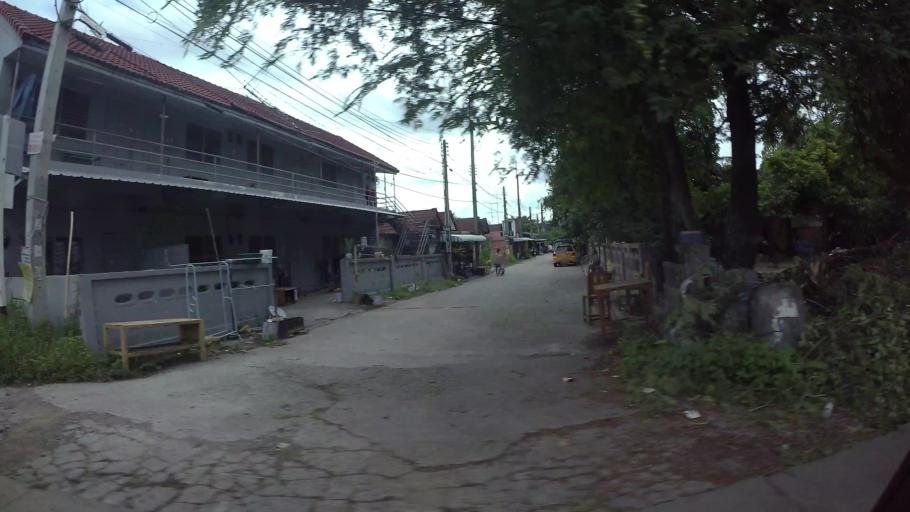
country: TH
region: Chon Buri
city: Ban Talat Bueng
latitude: 13.1193
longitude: 100.9731
